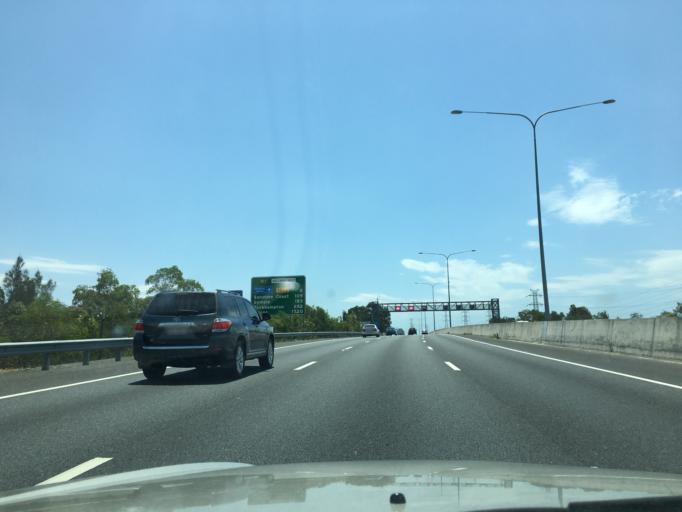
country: AU
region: Queensland
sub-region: Brisbane
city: Cannon Hill
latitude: -27.4760
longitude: 153.1167
